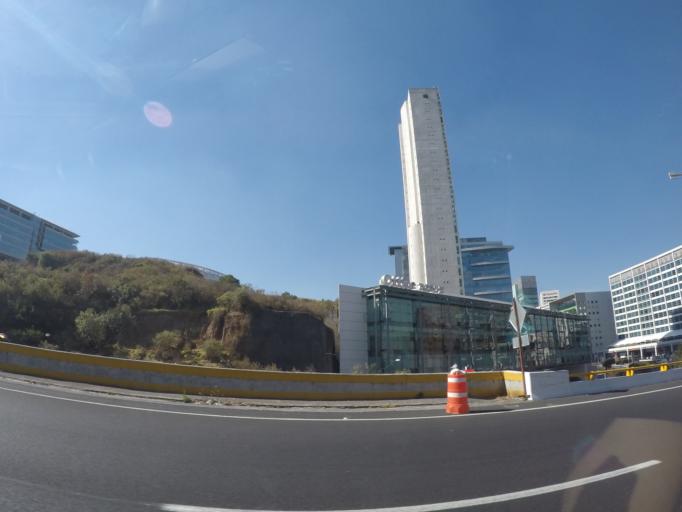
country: MX
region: Mexico City
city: Cuajimalpa
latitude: 19.3571
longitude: -99.2771
